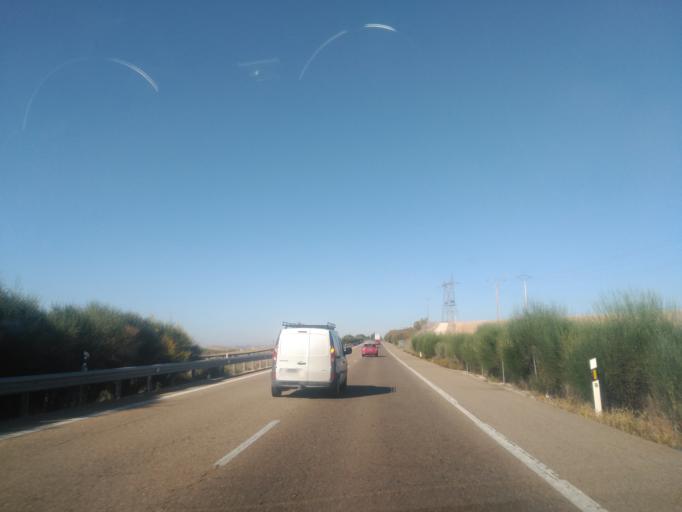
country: ES
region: Castille and Leon
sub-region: Provincia de Valladolid
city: Cisterniga
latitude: 41.5972
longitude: -4.6421
